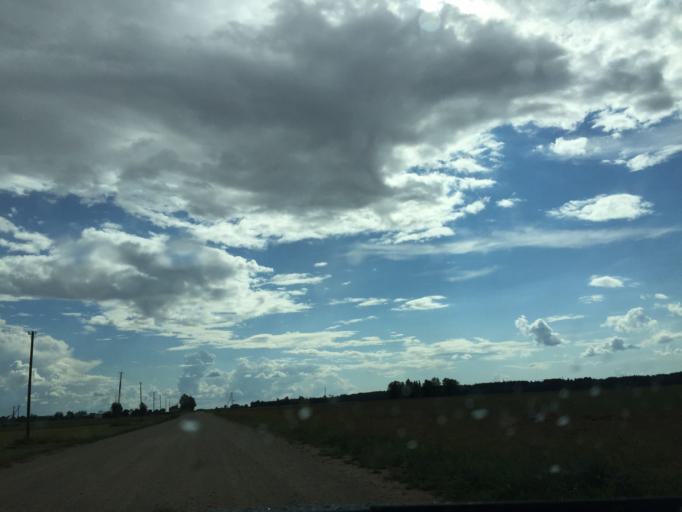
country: LT
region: Siauliu apskritis
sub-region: Joniskis
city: Joniskis
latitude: 56.3309
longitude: 23.5621
